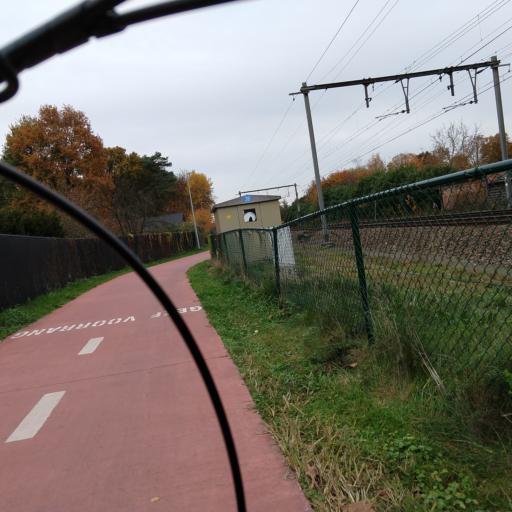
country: BE
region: Flanders
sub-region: Provincie Antwerpen
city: Kalmthout
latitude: 51.3747
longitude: 4.4659
